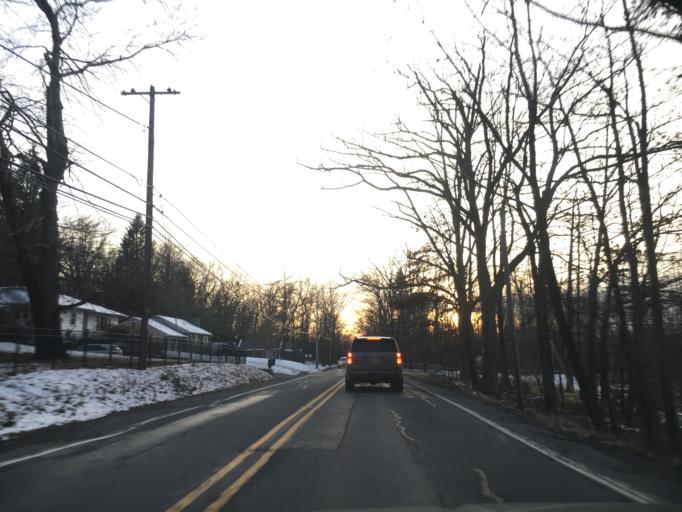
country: US
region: Pennsylvania
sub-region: Monroe County
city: East Stroudsburg
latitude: 41.0571
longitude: -75.1230
